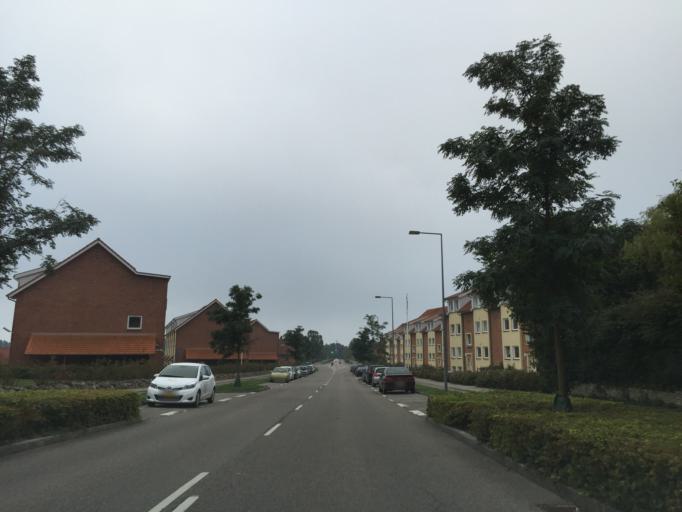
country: DK
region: South Denmark
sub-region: Sonderborg Kommune
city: Sonderborg
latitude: 54.9072
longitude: 9.8034
